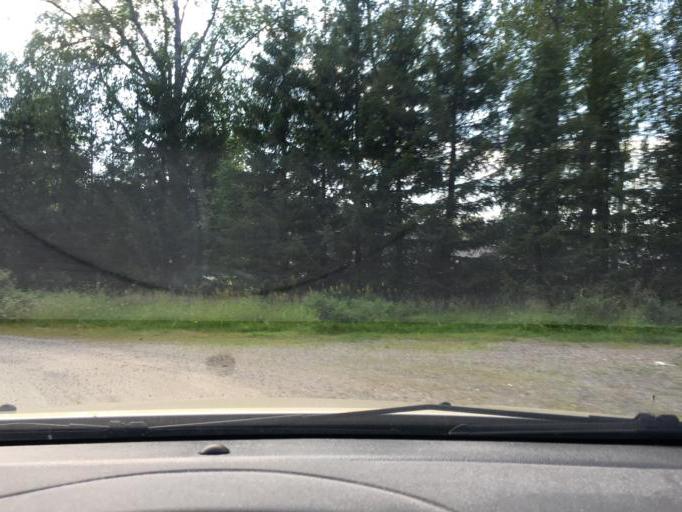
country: SE
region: Norrbotten
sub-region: Kalix Kommun
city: Toere
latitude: 66.0698
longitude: 22.7010
